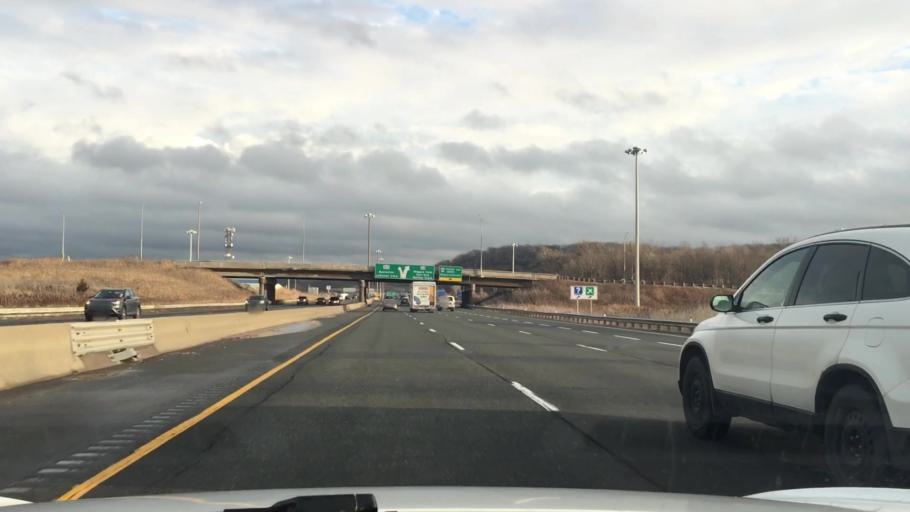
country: CA
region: Ontario
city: Thorold
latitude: 43.1578
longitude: -79.1663
